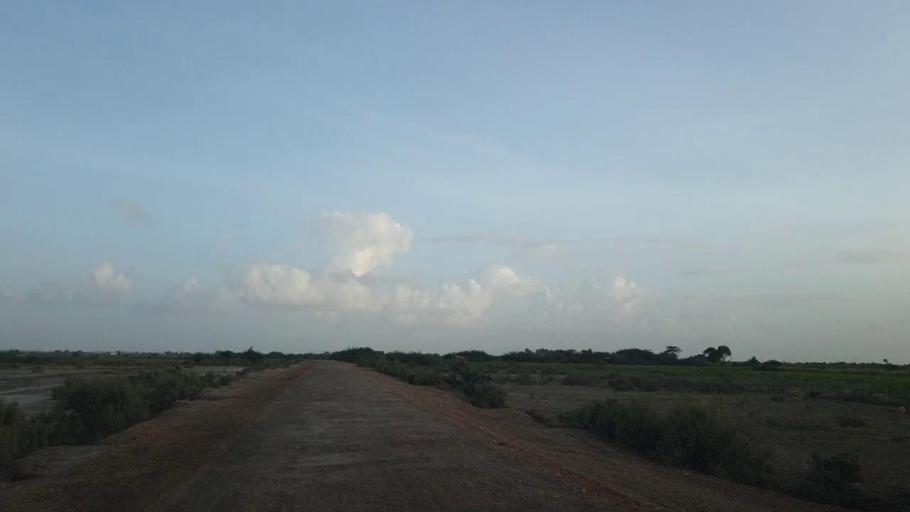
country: PK
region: Sindh
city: Kadhan
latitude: 24.5598
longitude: 69.1215
